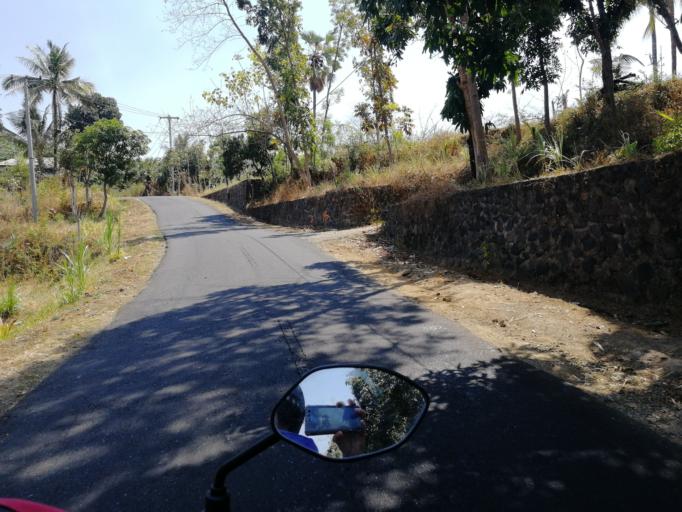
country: ID
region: Bali
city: Banjar Trunyan
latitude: -8.1286
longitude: 115.3249
